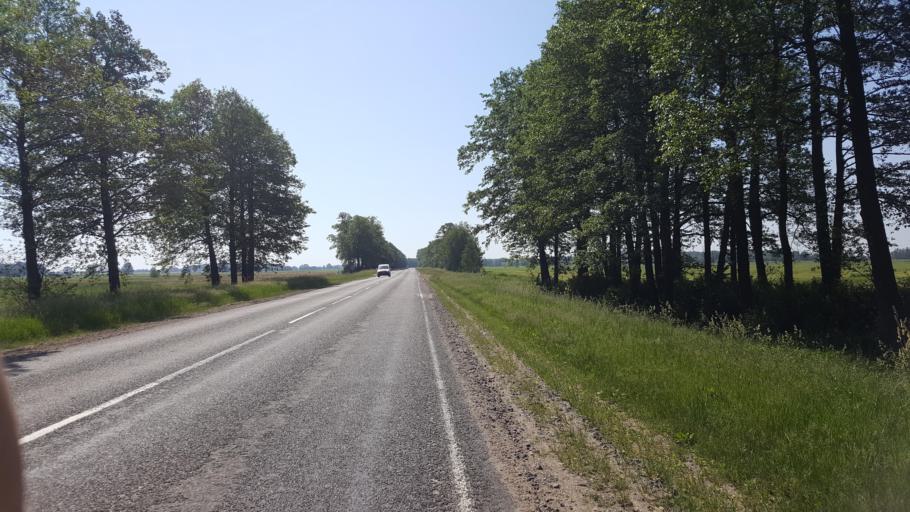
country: BY
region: Brest
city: Zhabinka
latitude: 52.3067
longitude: 23.9260
